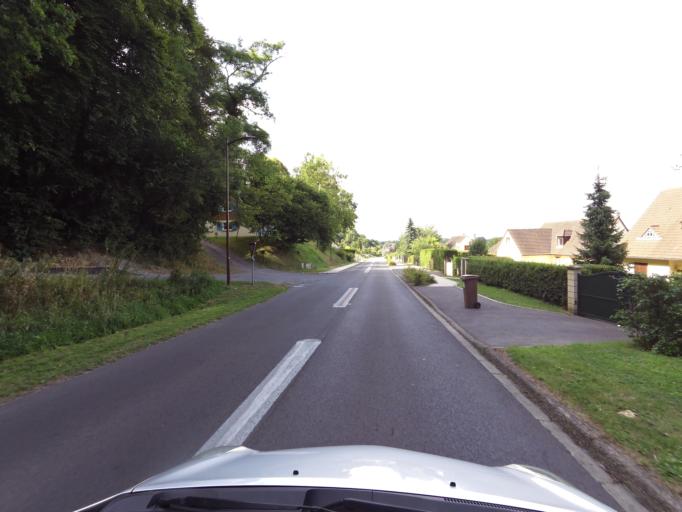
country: FR
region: Picardie
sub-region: Departement de l'Aisne
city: Bruyeres-et-Montberault
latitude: 49.5166
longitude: 3.6679
